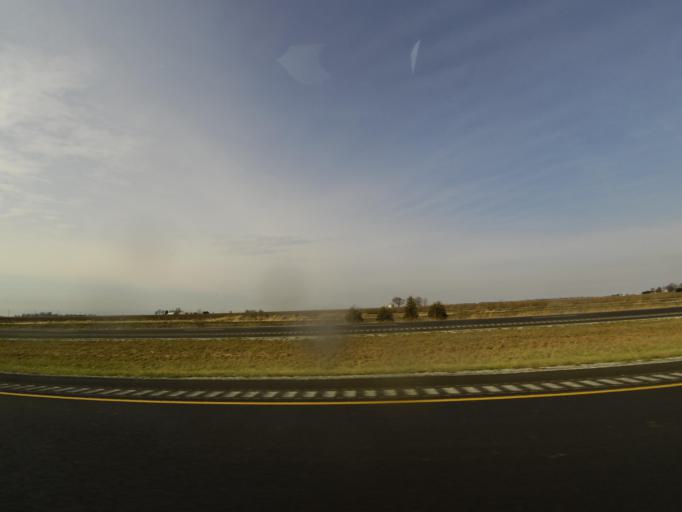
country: US
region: Illinois
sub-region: Macon County
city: Macon
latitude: 39.7307
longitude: -88.9922
